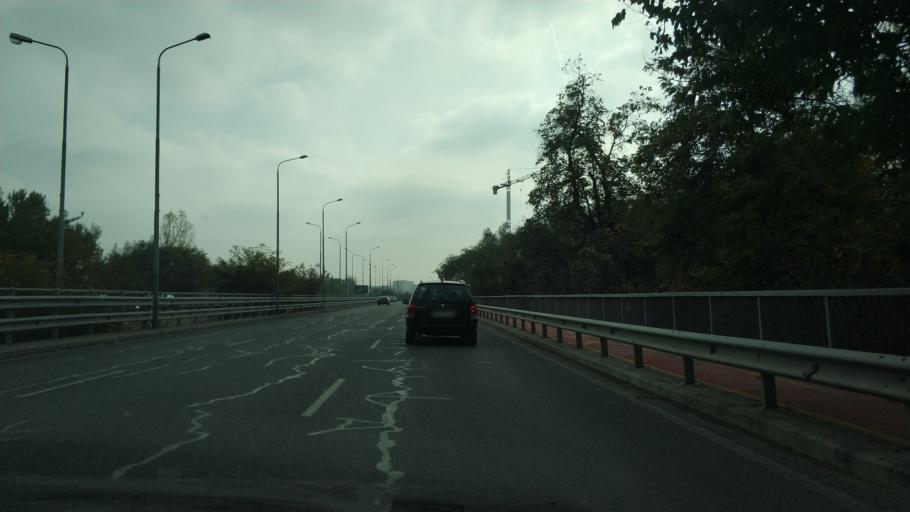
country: BG
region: Plovdiv
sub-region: Obshtina Plovdiv
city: Plovdiv
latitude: 42.1558
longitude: 24.7654
